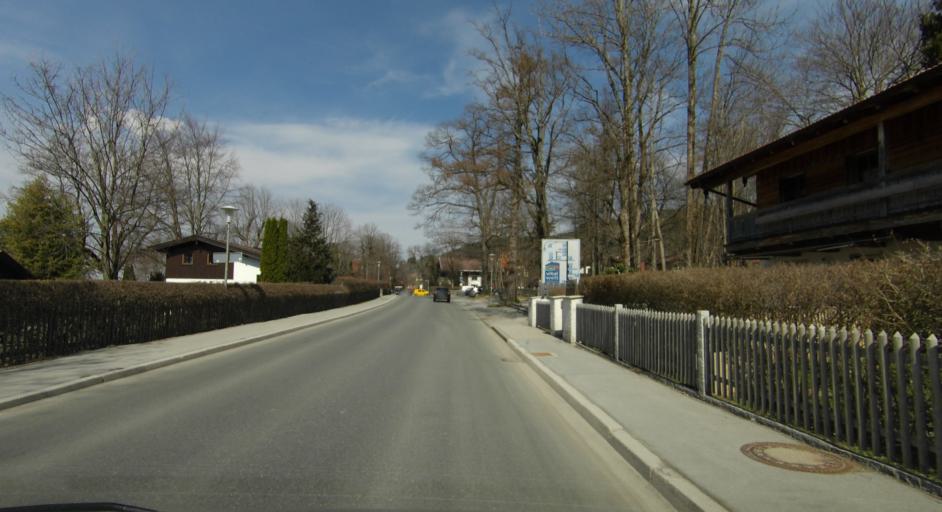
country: DE
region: Bavaria
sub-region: Upper Bavaria
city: Schliersee
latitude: 47.7259
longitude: 11.8696
